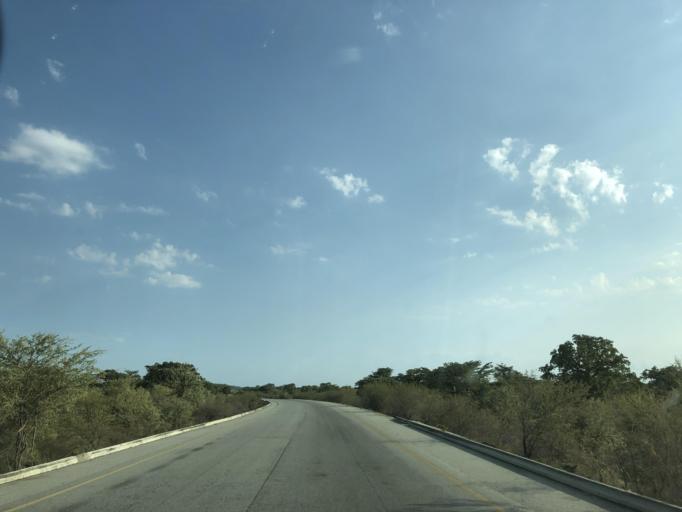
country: AO
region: Benguela
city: Benguela
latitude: -13.2082
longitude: 13.7639
